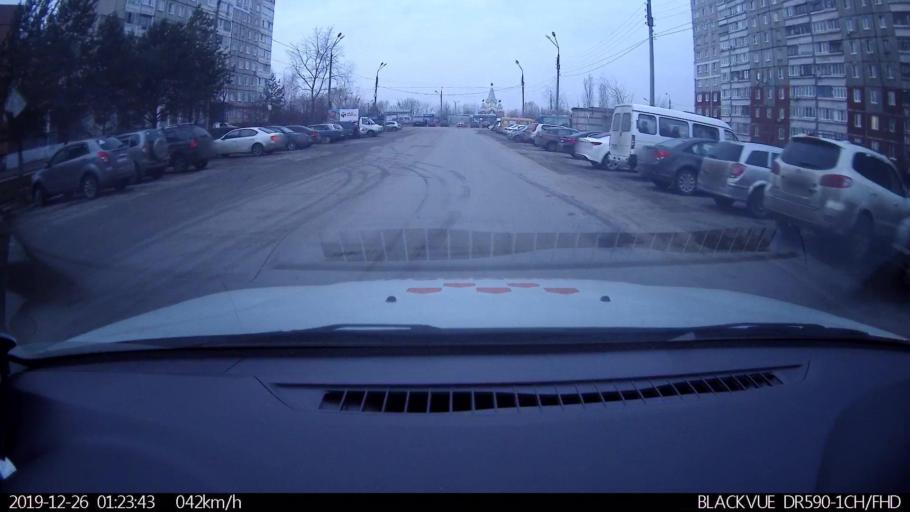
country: RU
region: Nizjnij Novgorod
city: Nizhniy Novgorod
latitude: 56.2735
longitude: 43.8832
